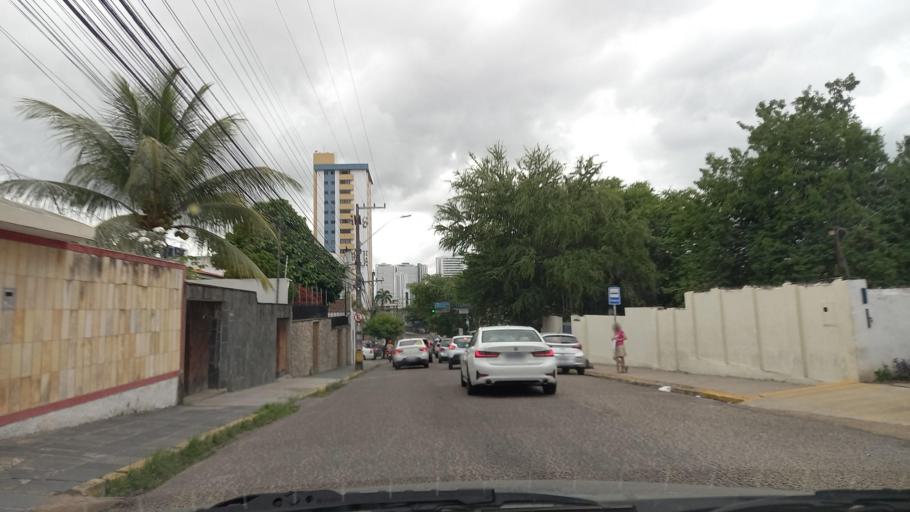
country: BR
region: Pernambuco
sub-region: Caruaru
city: Caruaru
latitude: -8.2797
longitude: -35.9688
